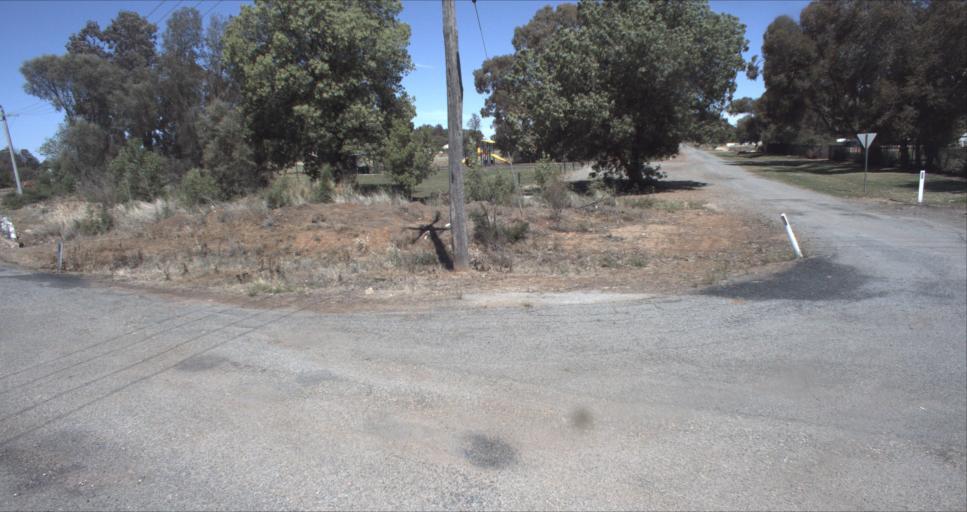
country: AU
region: New South Wales
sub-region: Leeton
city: Leeton
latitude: -34.5252
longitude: 146.3316
